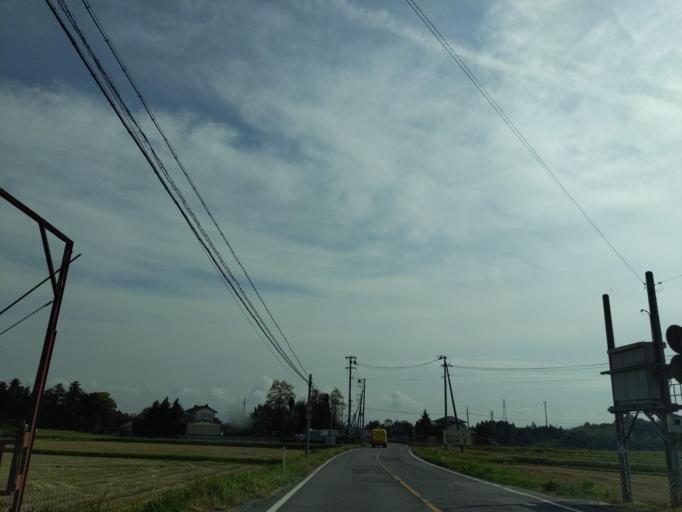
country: JP
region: Fukushima
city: Koriyama
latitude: 37.4185
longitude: 140.3227
